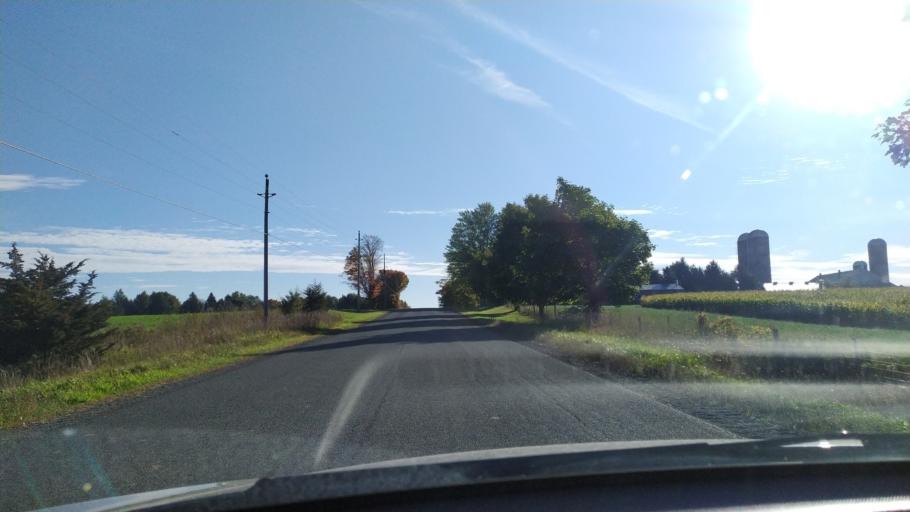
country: CA
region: Ontario
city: Stratford
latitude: 43.4618
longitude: -80.8238
